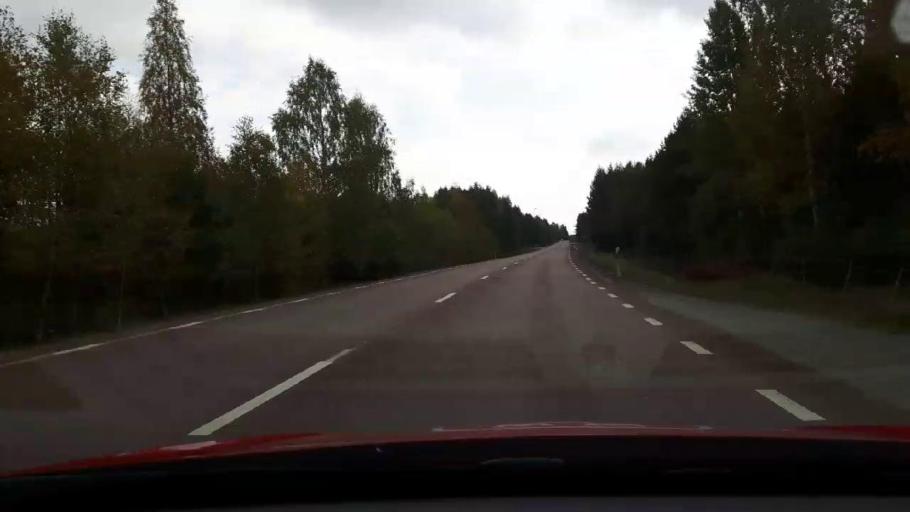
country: SE
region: Gaevleborg
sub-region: Bollnas Kommun
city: Kilafors
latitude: 61.2693
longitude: 16.5415
